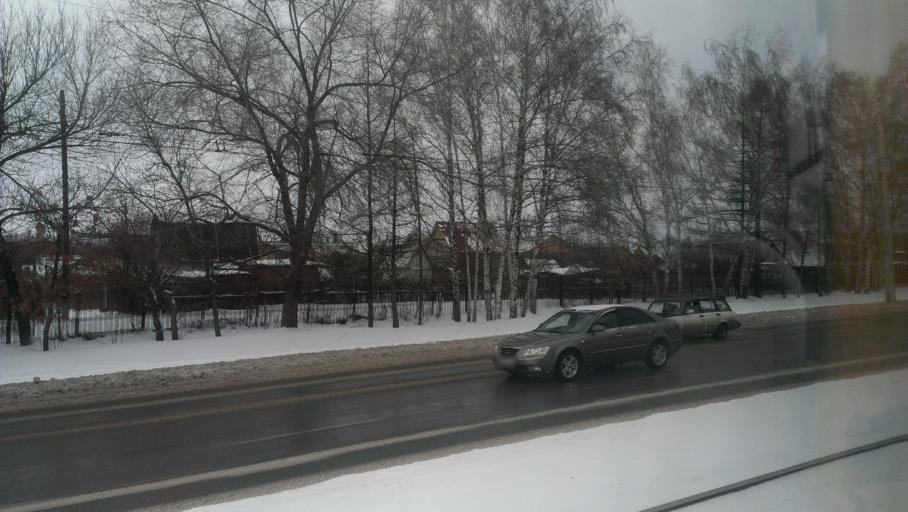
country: RU
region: Altai Krai
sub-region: Gorod Barnaulskiy
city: Barnaul
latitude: 53.3806
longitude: 83.7131
